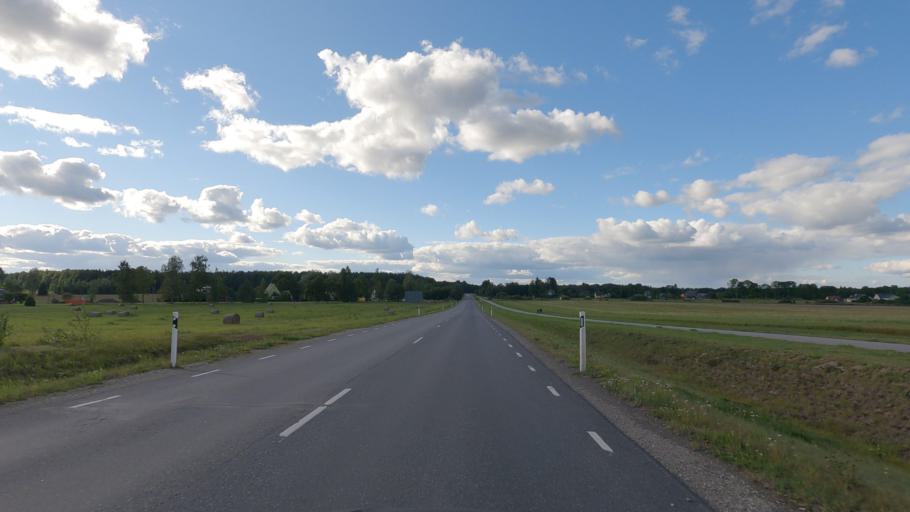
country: EE
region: Jaervamaa
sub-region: Tueri vald
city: Tueri
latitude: 58.8150
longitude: 25.4002
